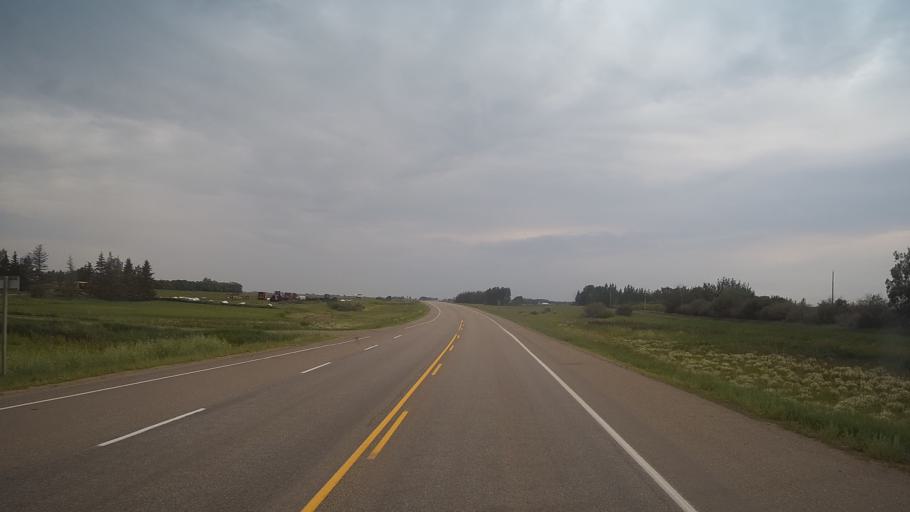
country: CA
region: Saskatchewan
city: Langham
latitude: 52.1289
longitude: -107.2310
